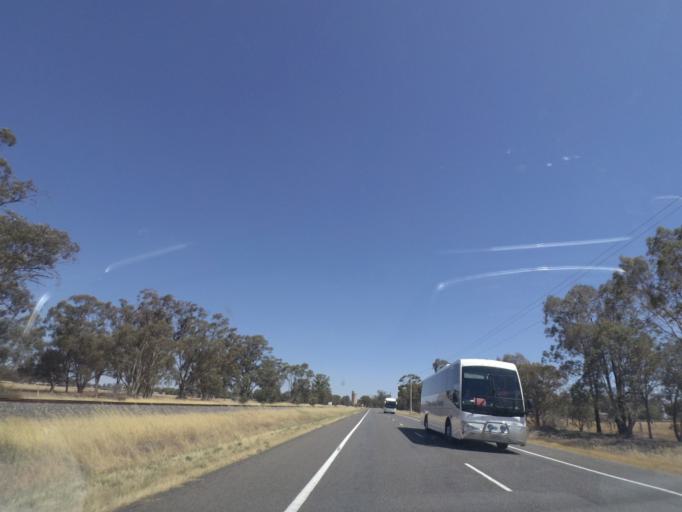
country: AU
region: Victoria
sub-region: Greater Shepparton
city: Shepparton
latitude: -36.2312
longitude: 145.4318
